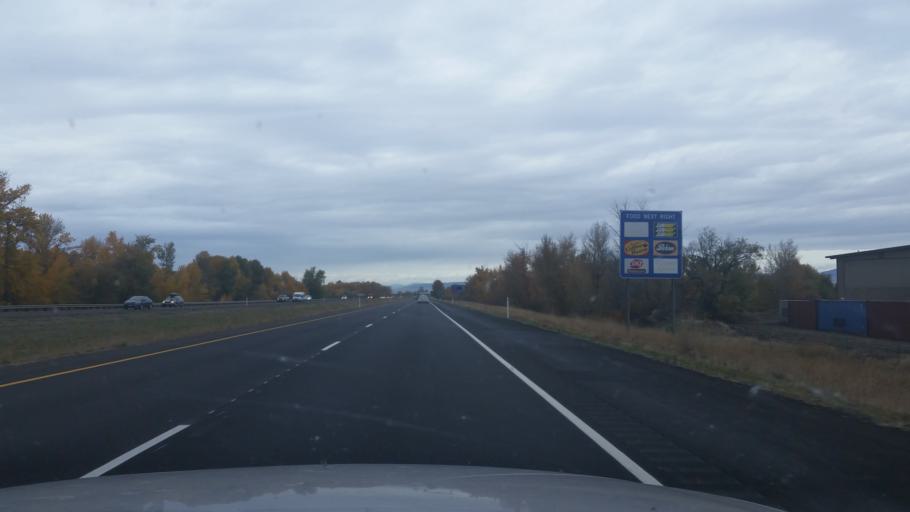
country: US
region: Washington
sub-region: Kittitas County
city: Ellensburg
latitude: 46.9956
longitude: -120.5779
